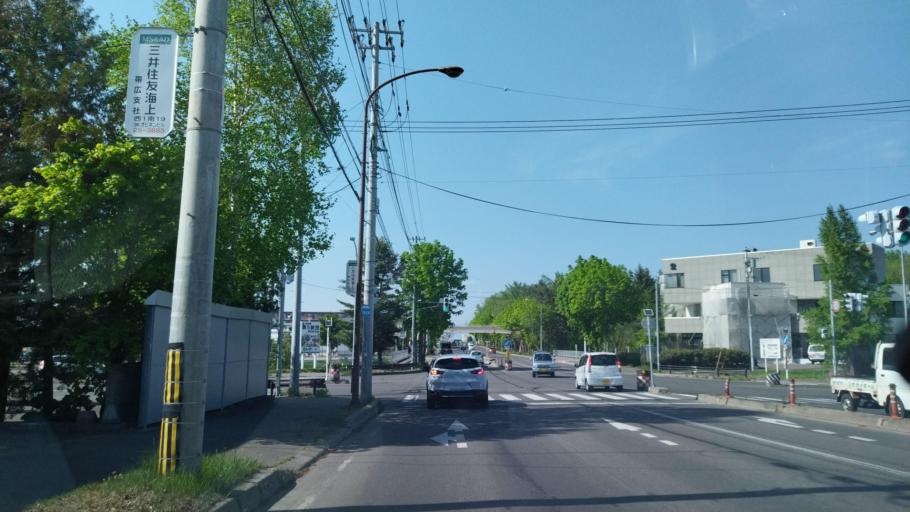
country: JP
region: Hokkaido
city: Obihiro
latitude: 42.8971
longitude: 143.1813
